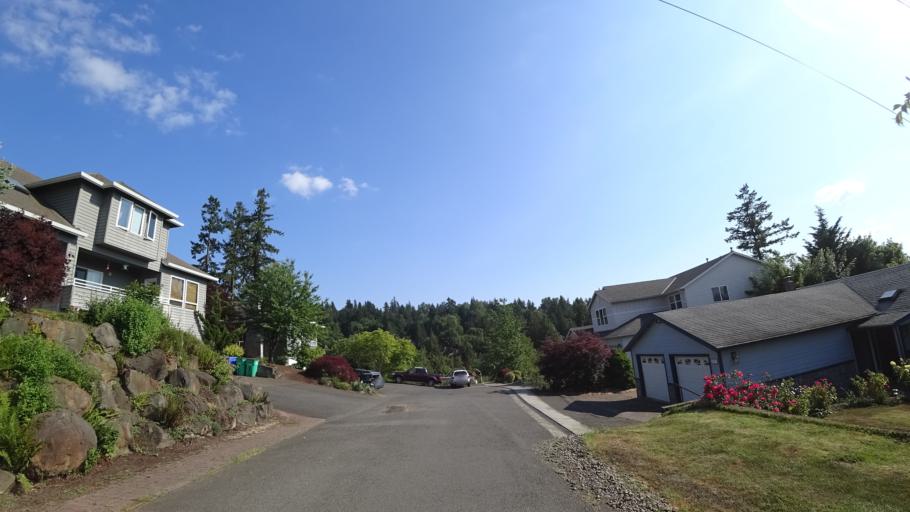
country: US
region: Oregon
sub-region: Washington County
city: Garden Home-Whitford
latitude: 45.4624
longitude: -122.7391
